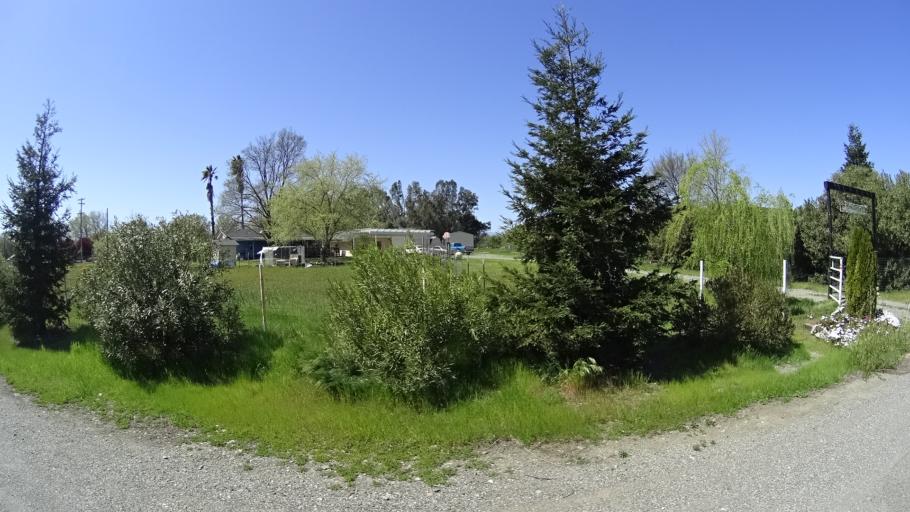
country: US
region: California
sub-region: Glenn County
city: Orland
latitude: 39.7775
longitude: -122.2386
